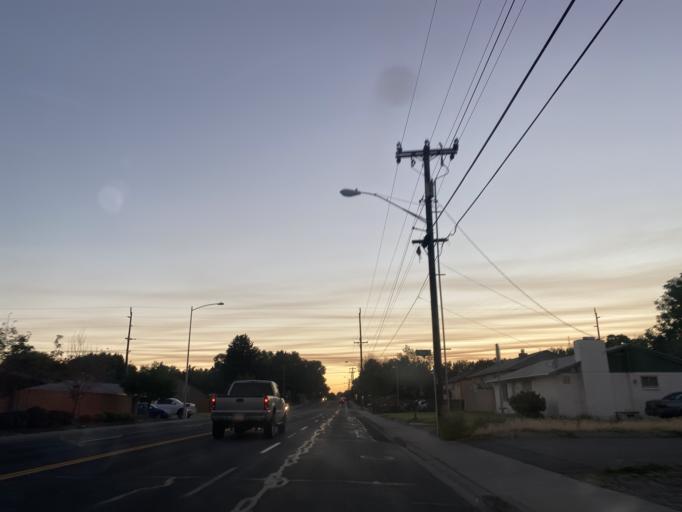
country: US
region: Washington
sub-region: Benton County
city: Kennewick
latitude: 46.1991
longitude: -119.1680
